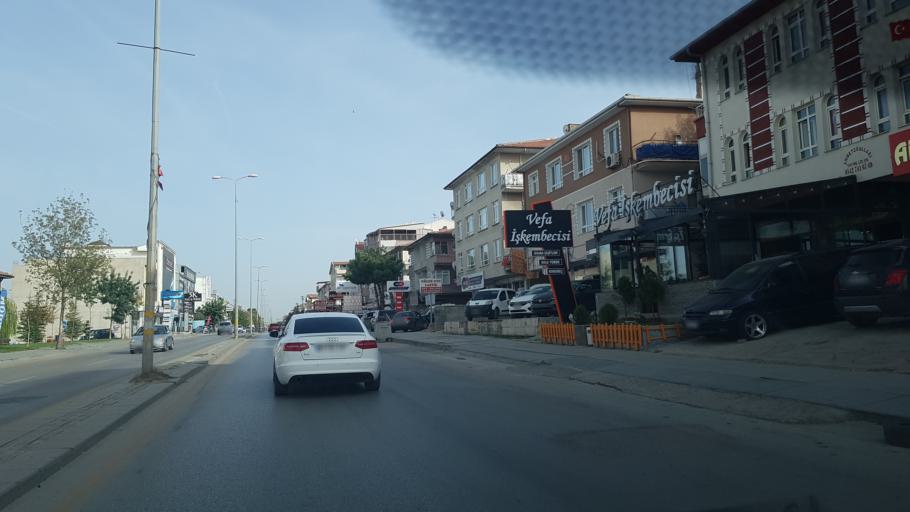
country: TR
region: Ankara
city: Etimesgut
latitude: 39.9502
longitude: 32.6540
